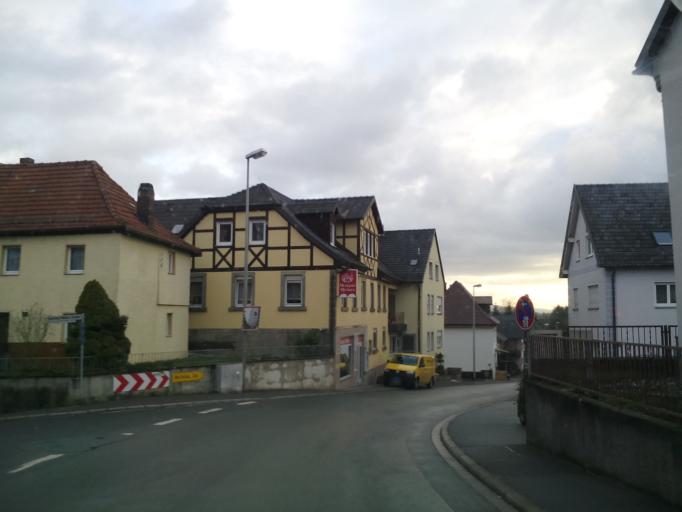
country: DE
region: Bavaria
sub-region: Upper Franconia
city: Lichtenfels
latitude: 50.1623
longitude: 11.0762
